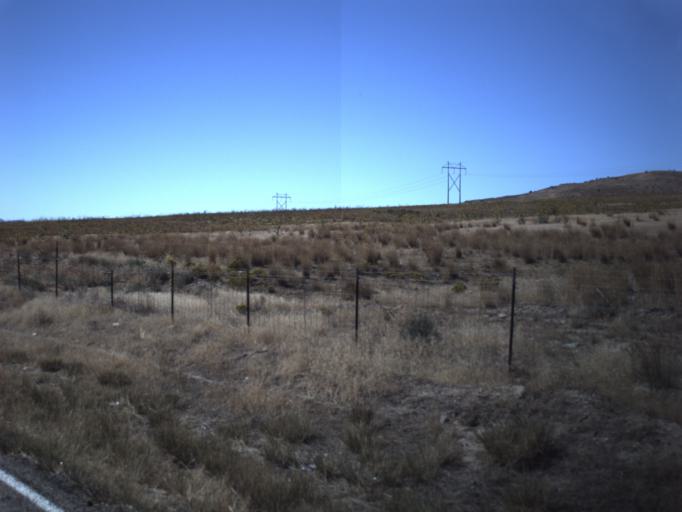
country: US
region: Utah
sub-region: Utah County
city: Saratoga Springs
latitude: 40.1925
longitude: -111.9056
